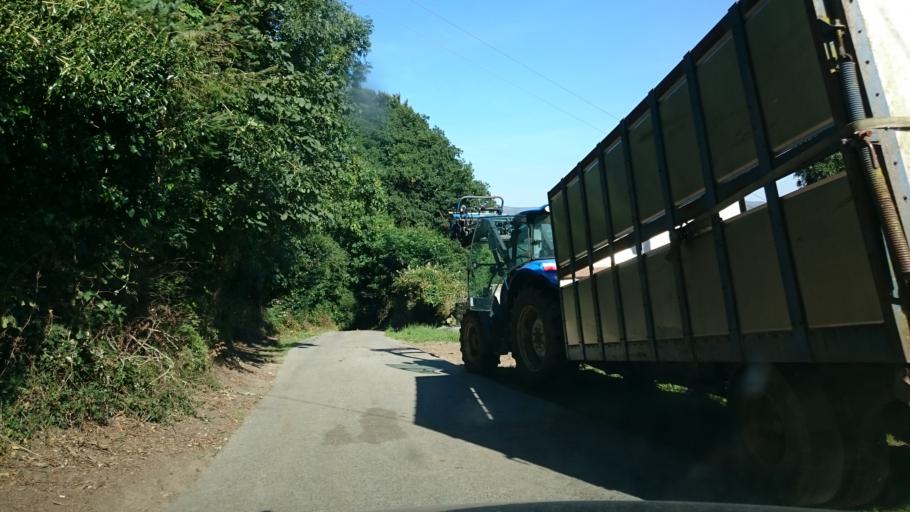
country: IE
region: Leinster
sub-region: Kilkenny
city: Graiguenamanagh
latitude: 52.5279
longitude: -6.9581
